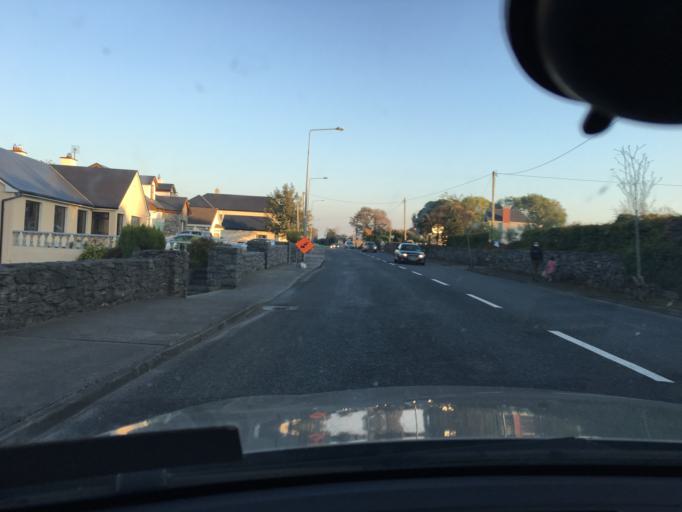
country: IE
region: Connaught
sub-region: County Galway
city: Moycullen
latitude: 53.3345
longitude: -9.1757
